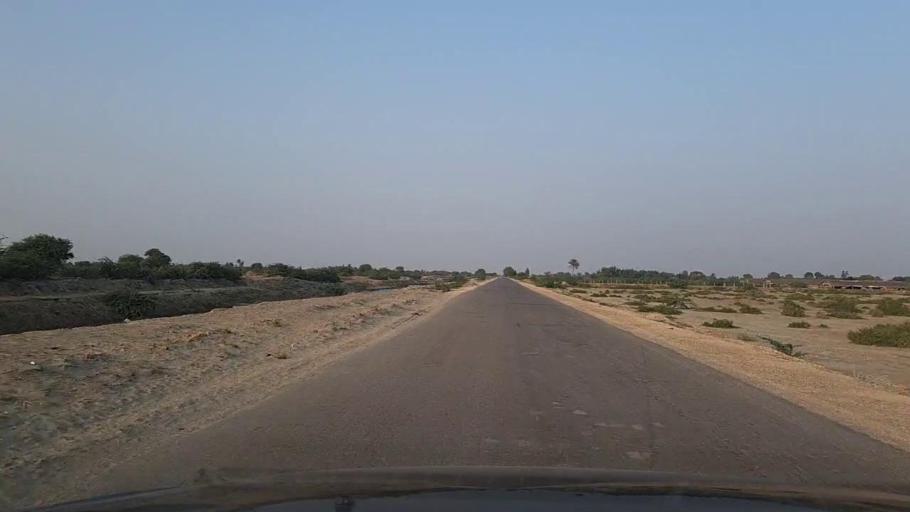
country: PK
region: Sindh
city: Mirpur Sakro
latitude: 24.4919
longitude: 67.8100
